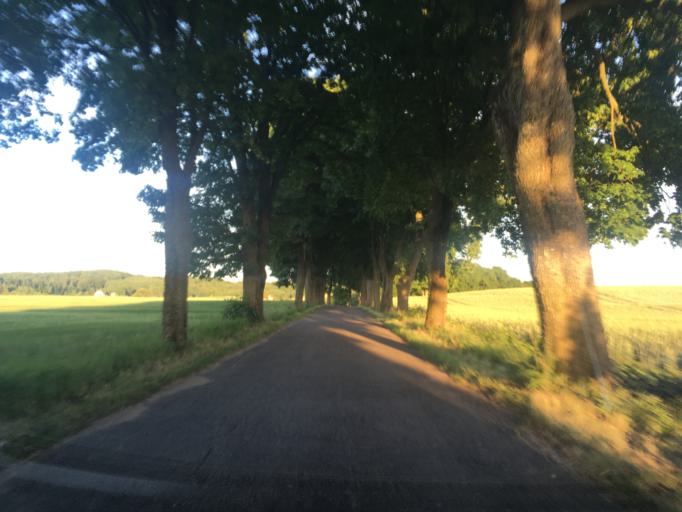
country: PL
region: Warmian-Masurian Voivodeship
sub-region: Powiat dzialdowski
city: Rybno
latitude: 53.5282
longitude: 19.9047
